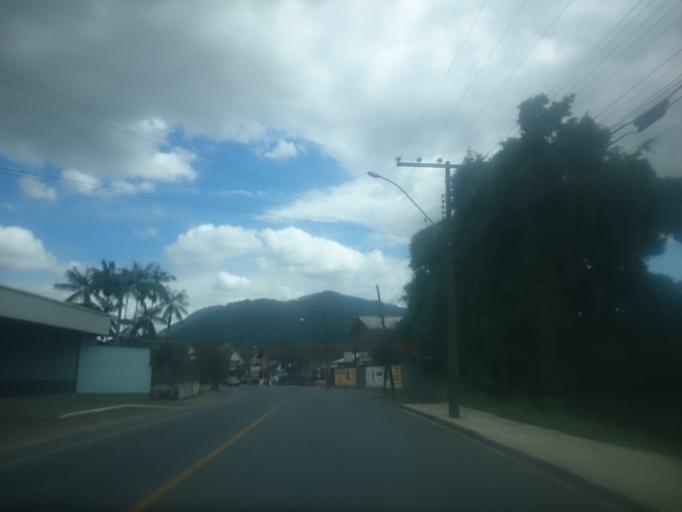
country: BR
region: Santa Catarina
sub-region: Pomerode
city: Pomerode
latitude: -26.7233
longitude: -49.1693
